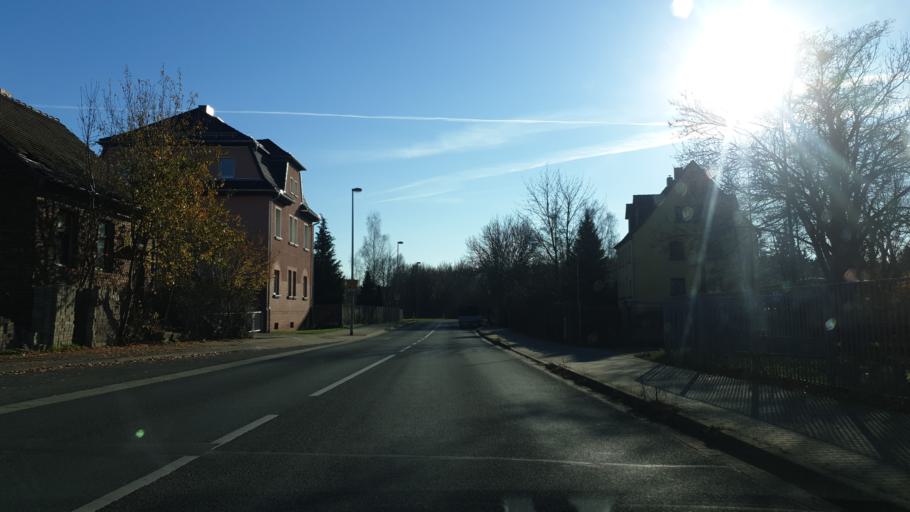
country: DE
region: Thuringia
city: Hartmannsdorf
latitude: 50.9652
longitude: 11.9835
